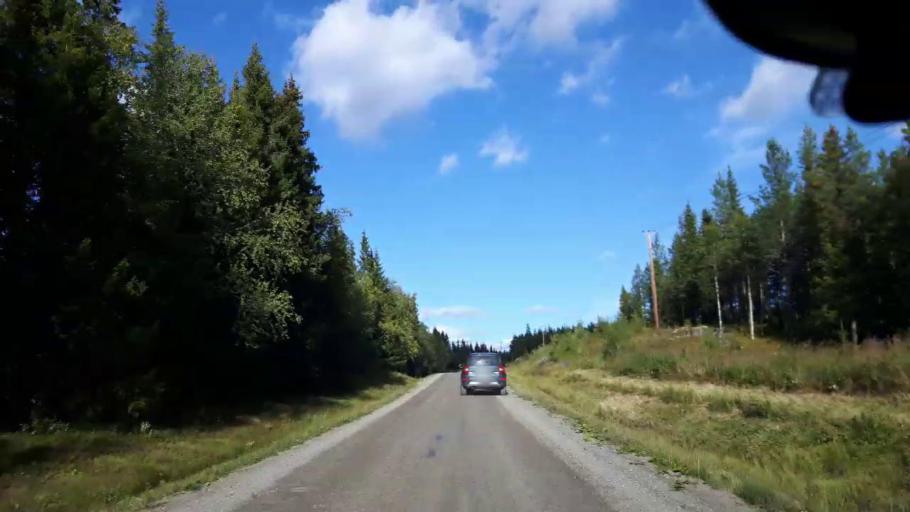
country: SE
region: Jaemtland
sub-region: Ragunda Kommun
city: Hammarstrand
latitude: 63.4157
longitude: 16.1028
